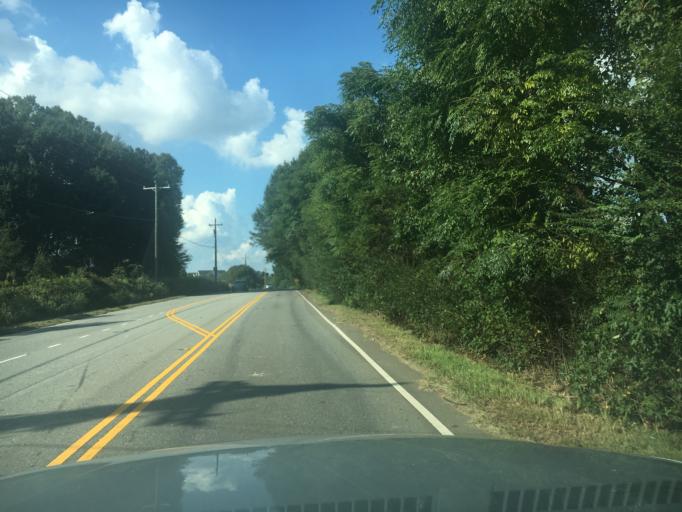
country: US
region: South Carolina
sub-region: Greenville County
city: Simpsonville
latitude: 34.6910
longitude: -82.2527
